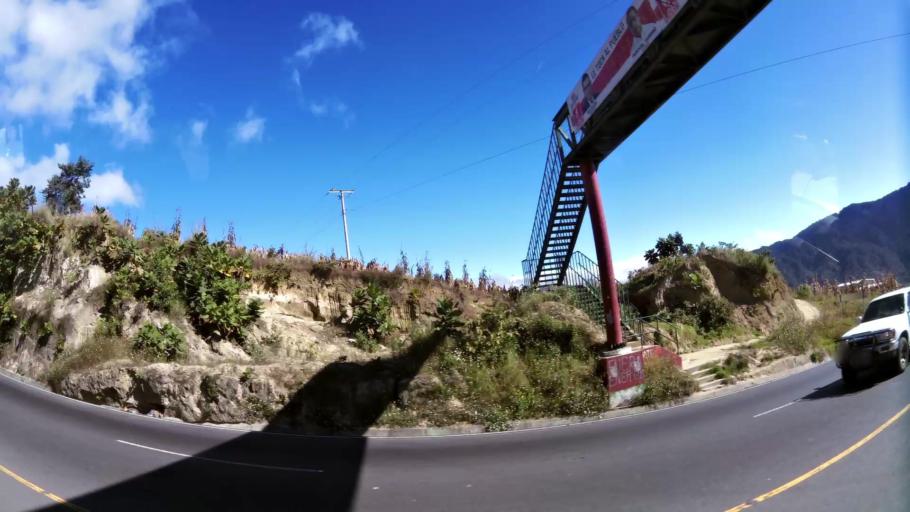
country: GT
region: Solola
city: Nahuala
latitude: 14.8192
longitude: -91.3356
